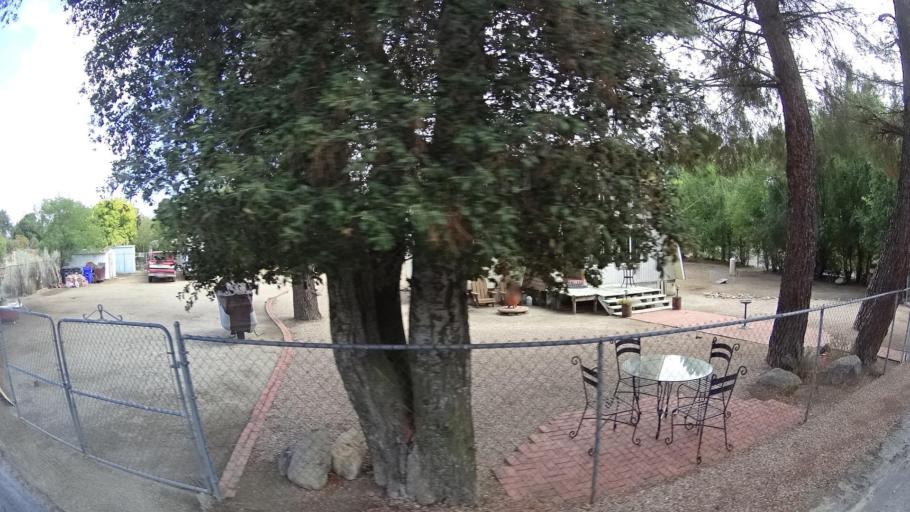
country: US
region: California
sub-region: San Diego County
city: Campo
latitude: 32.6863
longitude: -116.5146
